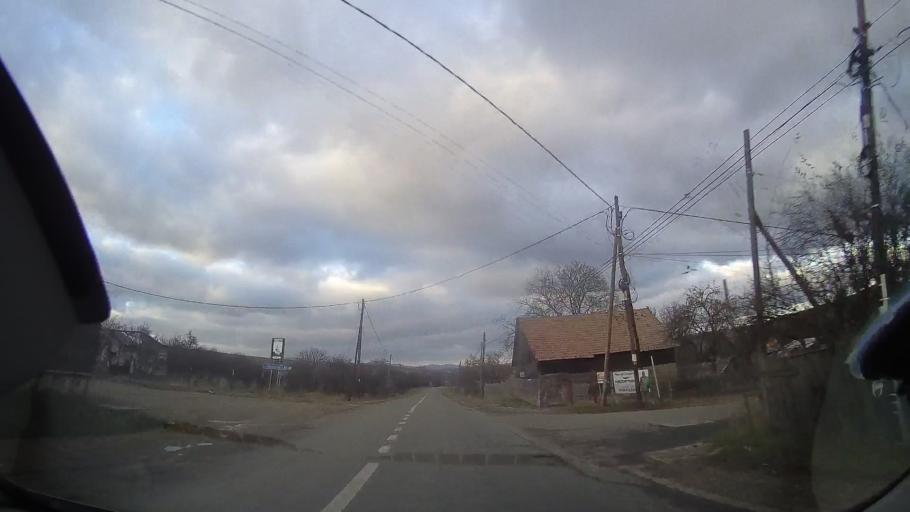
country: RO
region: Cluj
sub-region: Comuna Sancraiu
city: Sancraiu
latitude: 46.8035
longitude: 22.9949
